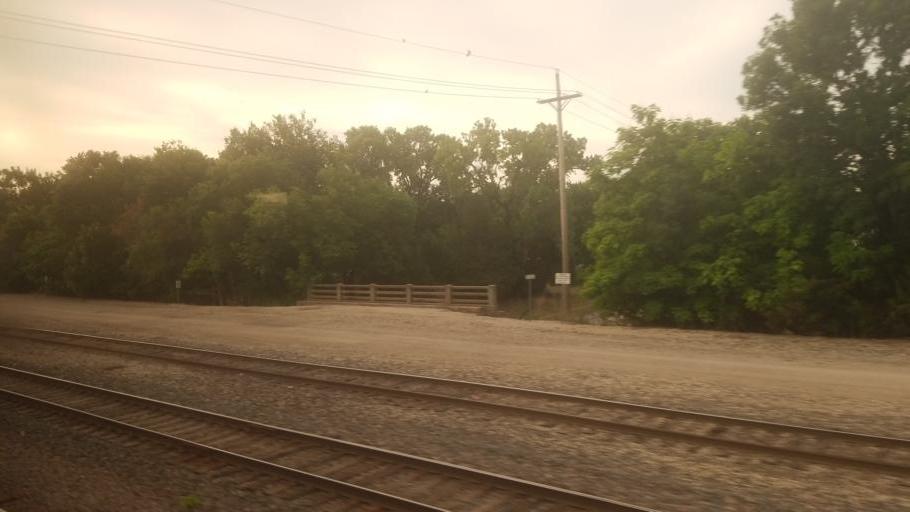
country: US
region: Kansas
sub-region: Lyon County
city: Emporia
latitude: 38.4013
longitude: -96.1857
